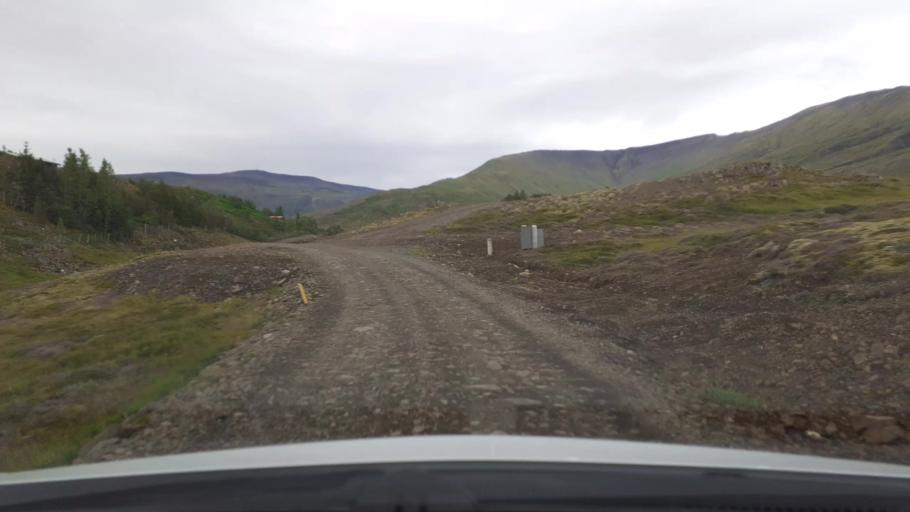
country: IS
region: Capital Region
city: Mosfellsbaer
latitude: 64.2872
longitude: -21.4624
